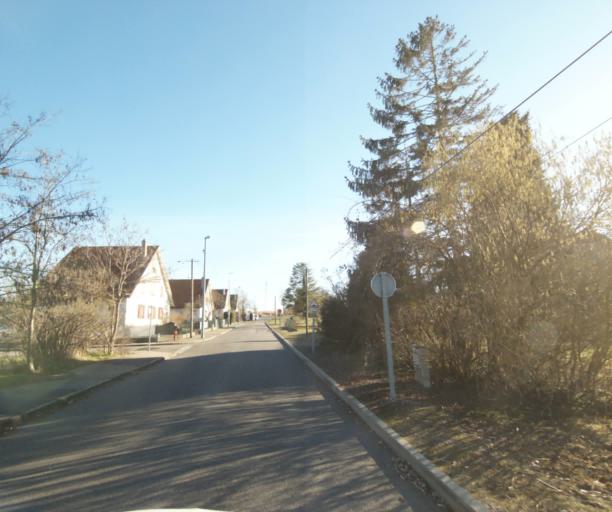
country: FR
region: Lorraine
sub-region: Departement de Meurthe-et-Moselle
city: Art-sur-Meurthe
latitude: 48.6379
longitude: 6.2700
